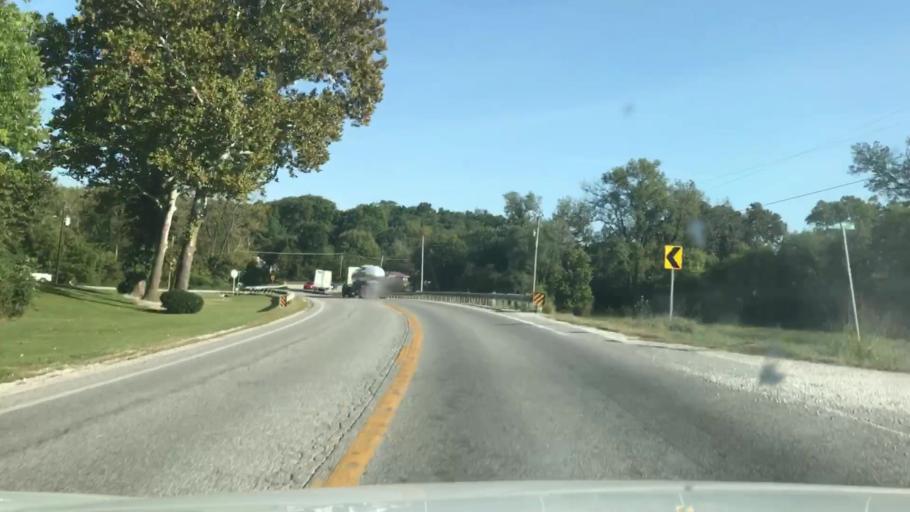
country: US
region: Illinois
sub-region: Adams County
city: Quincy
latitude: 39.8420
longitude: -91.3712
